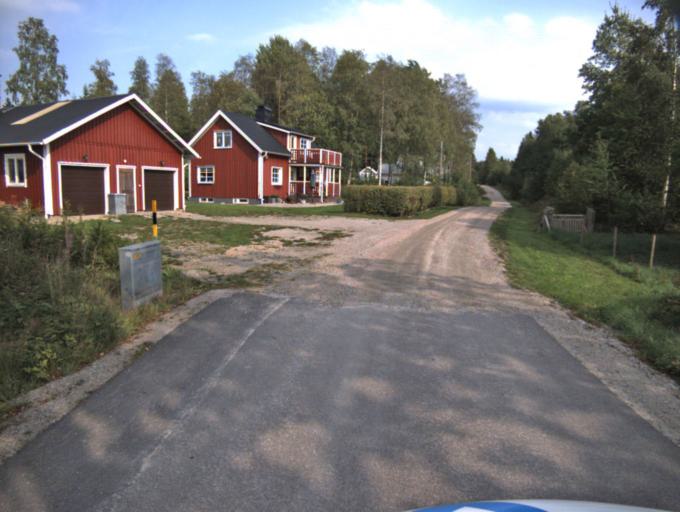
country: SE
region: Vaestra Goetaland
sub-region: Ulricehamns Kommun
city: Ulricehamn
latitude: 57.7788
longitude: 13.4300
